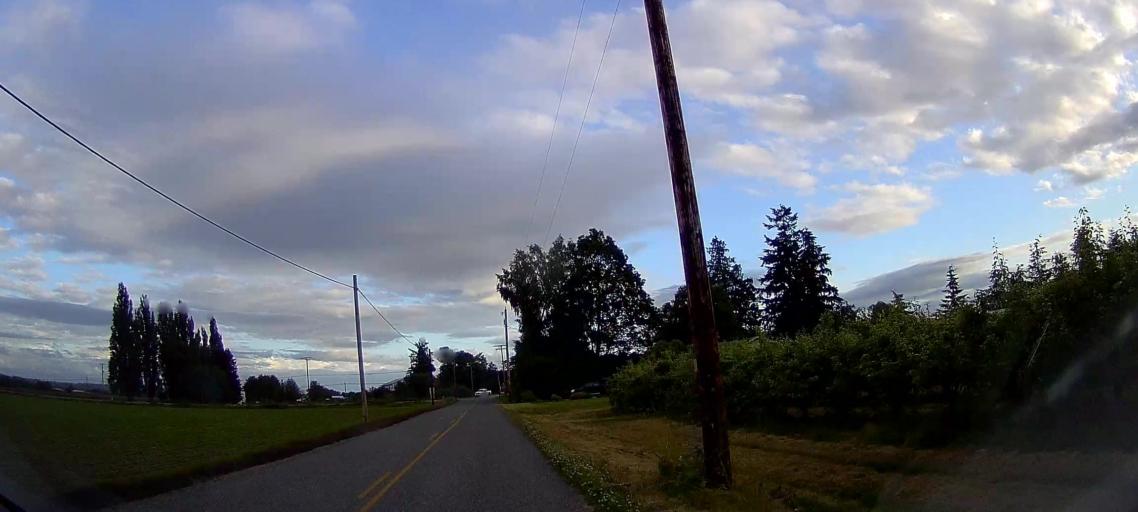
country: US
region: Washington
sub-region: Skagit County
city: Mount Vernon
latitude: 48.3425
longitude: -122.3897
